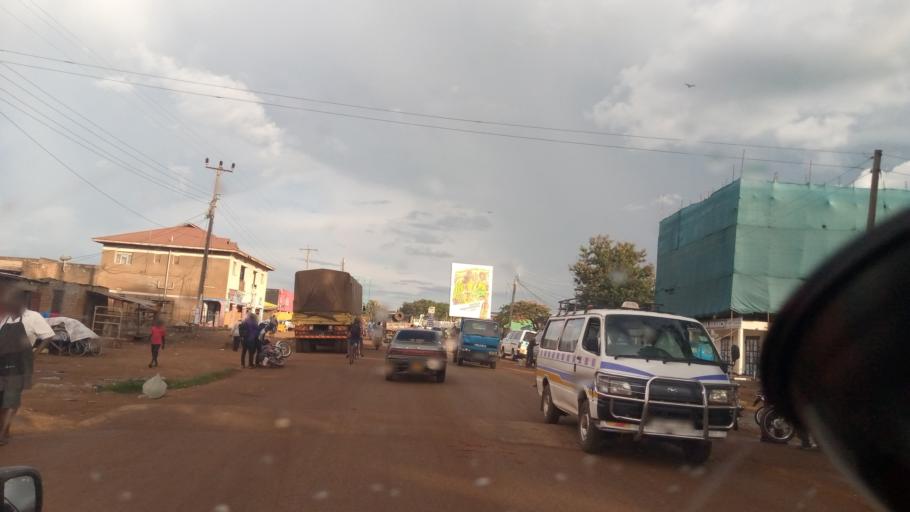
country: UG
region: Northern Region
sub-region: Lira District
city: Lira
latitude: 2.2378
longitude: 32.8904
